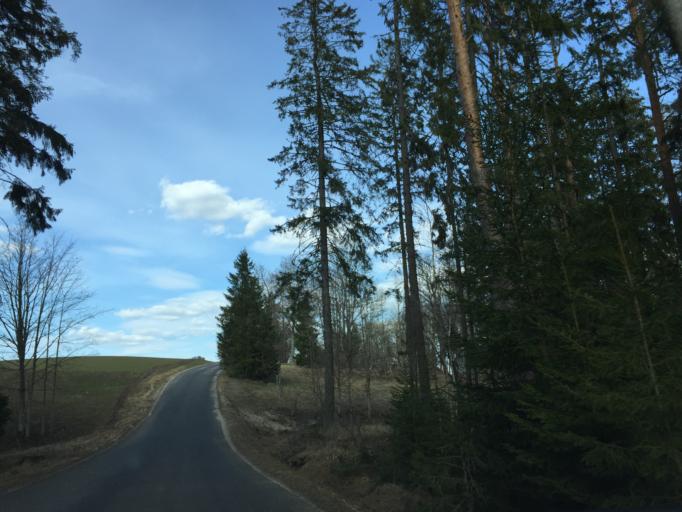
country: EE
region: Tartu
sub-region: Noo vald
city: Noo
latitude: 58.1267
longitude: 26.5790
